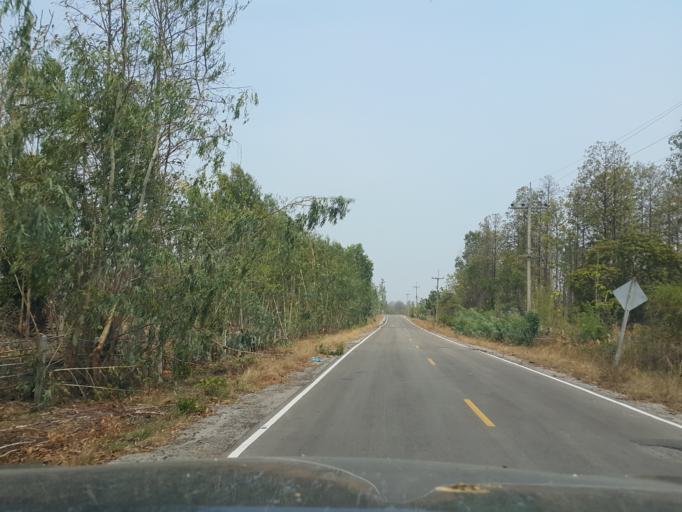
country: TH
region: Lampang
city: Mae Phrik
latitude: 17.5629
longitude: 99.0950
